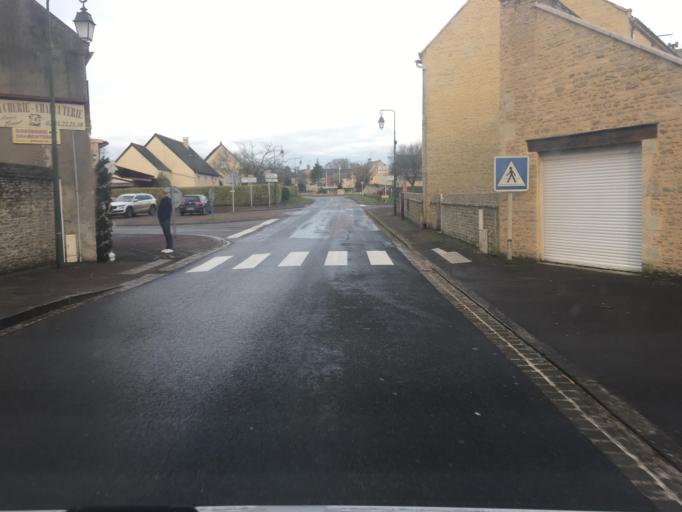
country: FR
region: Lower Normandy
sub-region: Departement du Calvados
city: Ver-sur-Mer
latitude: 49.3145
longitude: -0.5494
